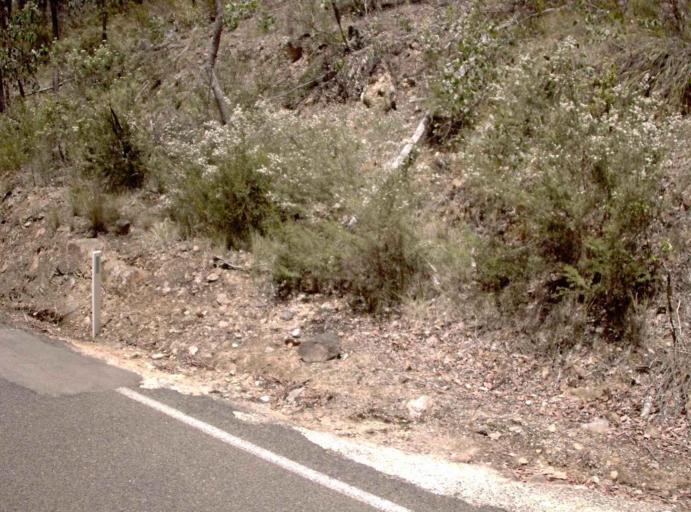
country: AU
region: Victoria
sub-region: East Gippsland
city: Lakes Entrance
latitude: -37.5751
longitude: 147.8953
